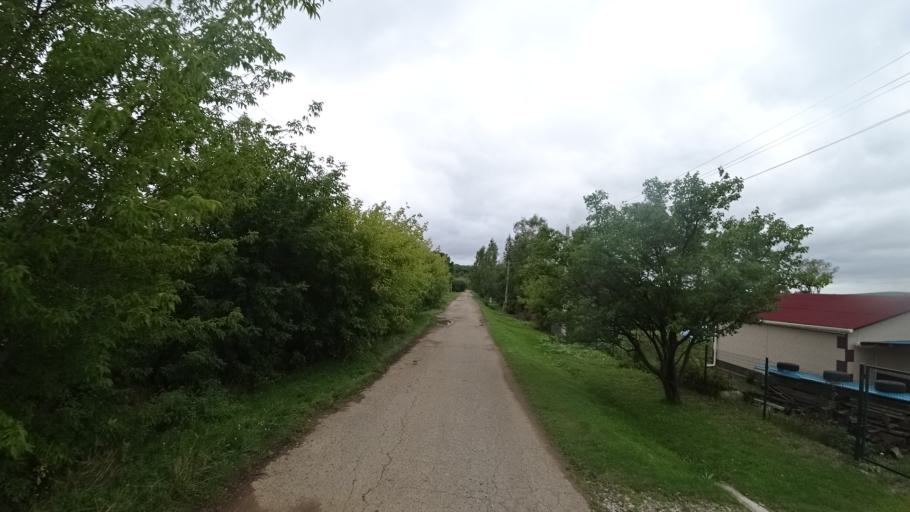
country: RU
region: Primorskiy
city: Chernigovka
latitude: 44.4560
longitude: 132.5929
